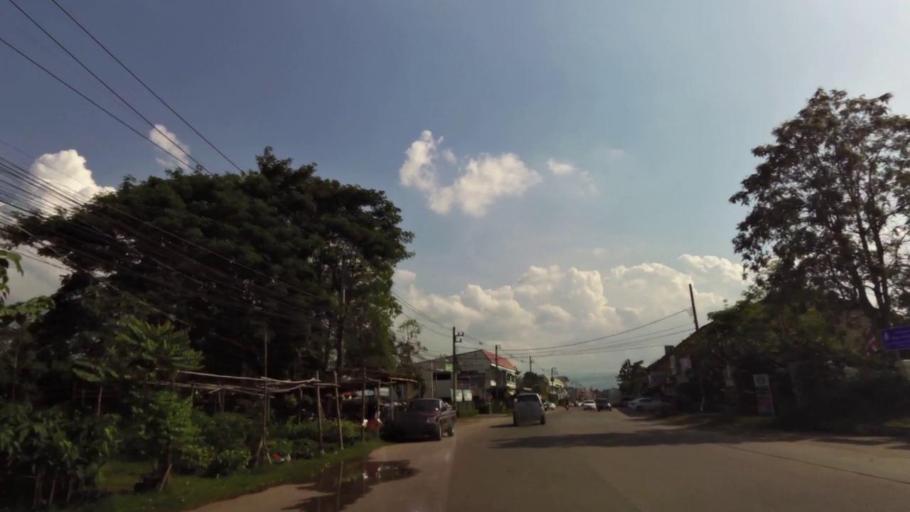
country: TH
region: Phrae
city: Phrae
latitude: 18.1237
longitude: 100.1526
